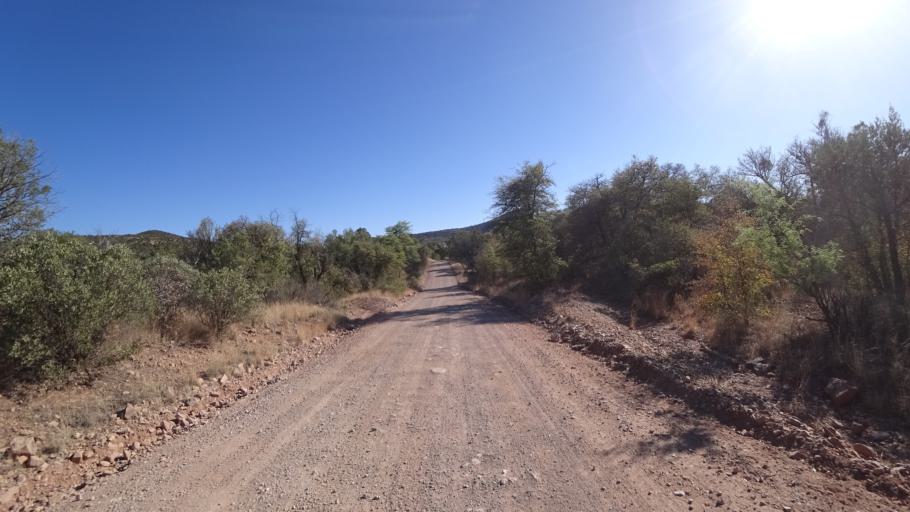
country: US
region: Arizona
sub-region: Cochise County
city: Huachuca City
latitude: 31.5211
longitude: -110.5487
